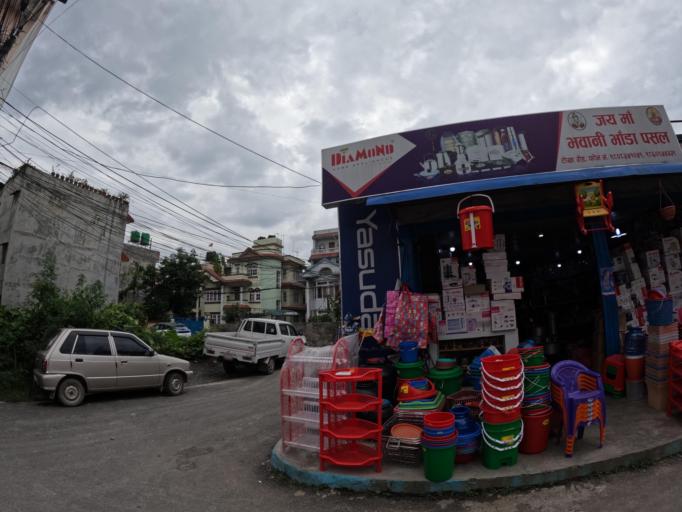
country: NP
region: Central Region
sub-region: Bagmati Zone
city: Kathmandu
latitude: 27.7435
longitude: 85.3217
